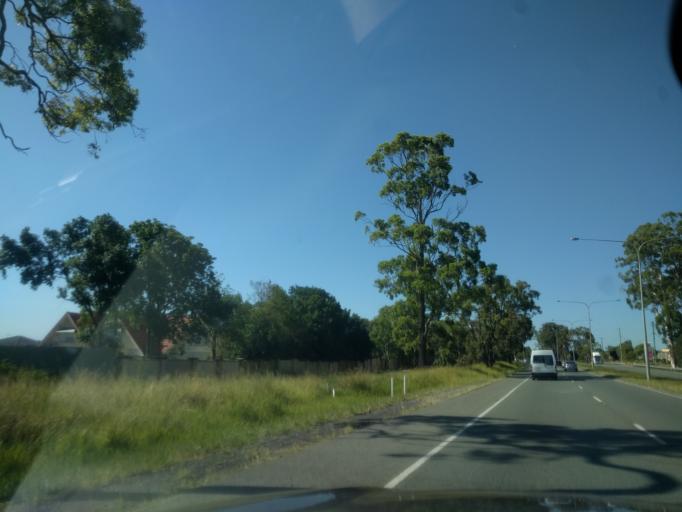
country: AU
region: Queensland
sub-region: Brisbane
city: Sunnybank Hills
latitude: -27.6345
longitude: 153.0459
